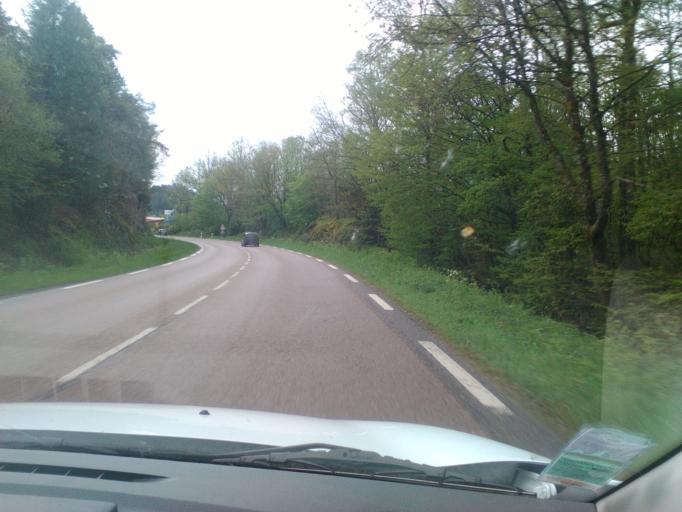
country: FR
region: Lorraine
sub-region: Departement des Vosges
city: Vagney
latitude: 47.9827
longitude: 6.7230
